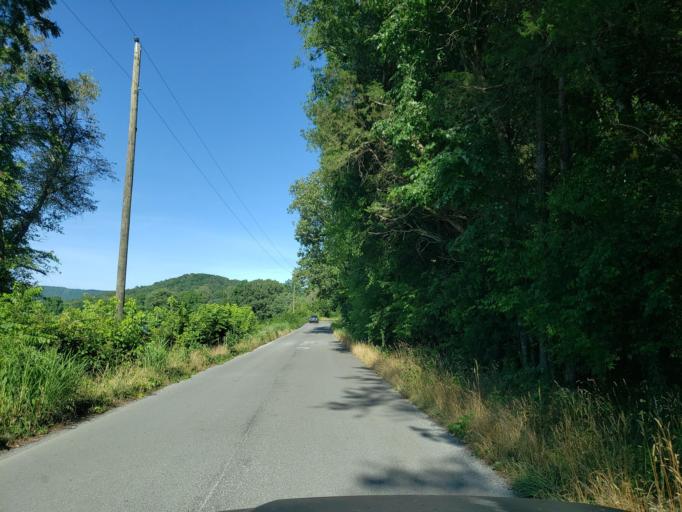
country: US
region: Georgia
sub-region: Whitfield County
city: Dalton
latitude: 34.6658
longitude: -85.1024
